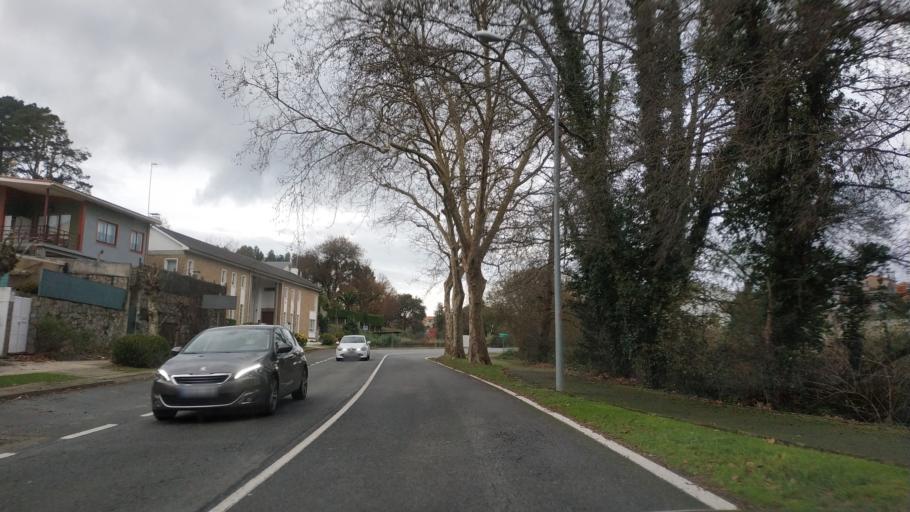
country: ES
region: Galicia
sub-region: Provincia da Coruna
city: Oleiros
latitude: 43.3506
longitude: -8.3409
